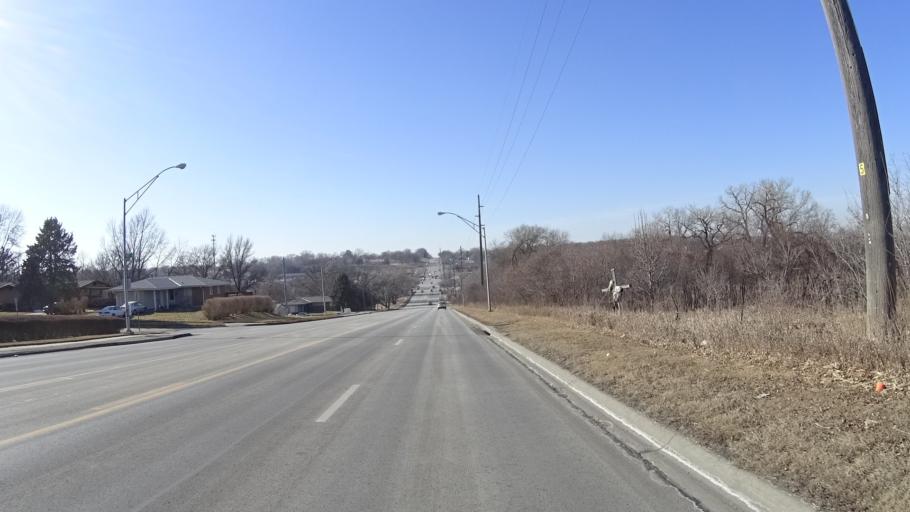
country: US
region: Nebraska
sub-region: Douglas County
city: Ralston
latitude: 41.3068
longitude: -96.0447
